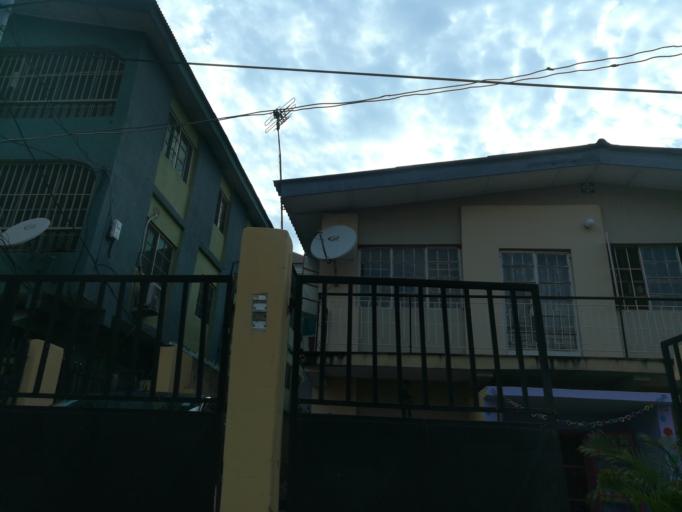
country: NG
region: Lagos
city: Ikeja
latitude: 6.5975
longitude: 3.3453
